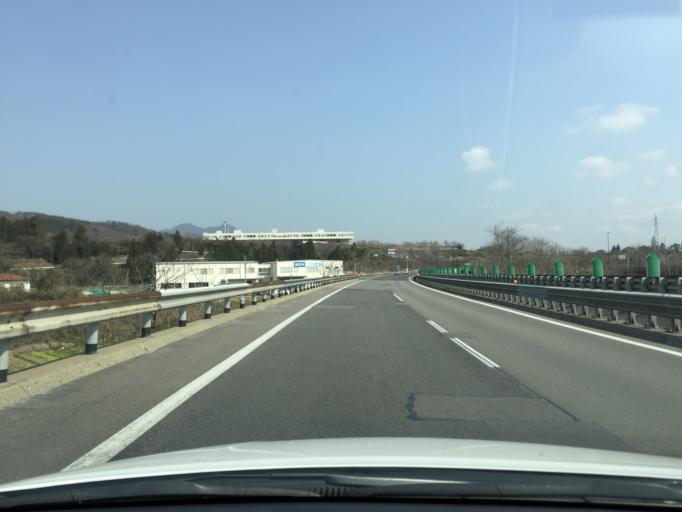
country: JP
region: Miyagi
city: Shiroishi
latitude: 38.0060
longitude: 140.6089
